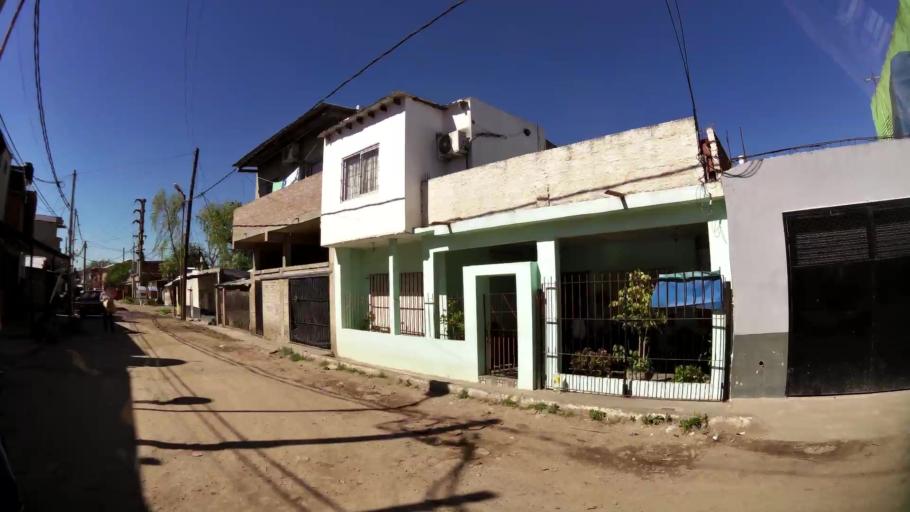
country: AR
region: Buenos Aires
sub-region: Partido de Quilmes
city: Quilmes
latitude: -34.7098
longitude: -58.3035
